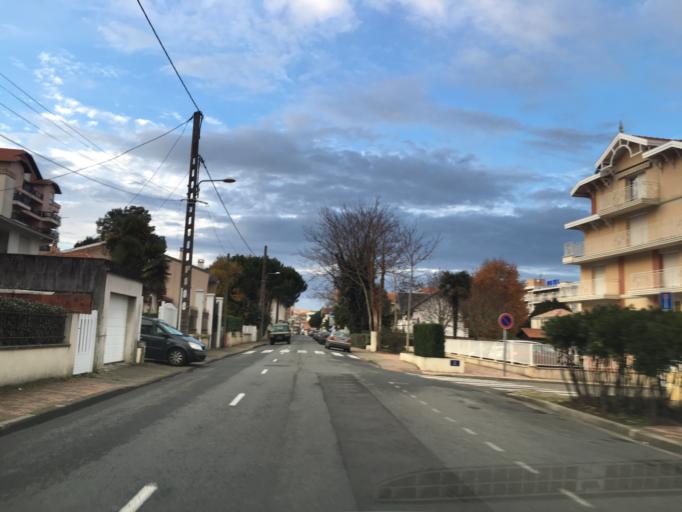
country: FR
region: Aquitaine
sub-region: Departement de la Gironde
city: Arcachon
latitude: 44.6606
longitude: -1.1548
